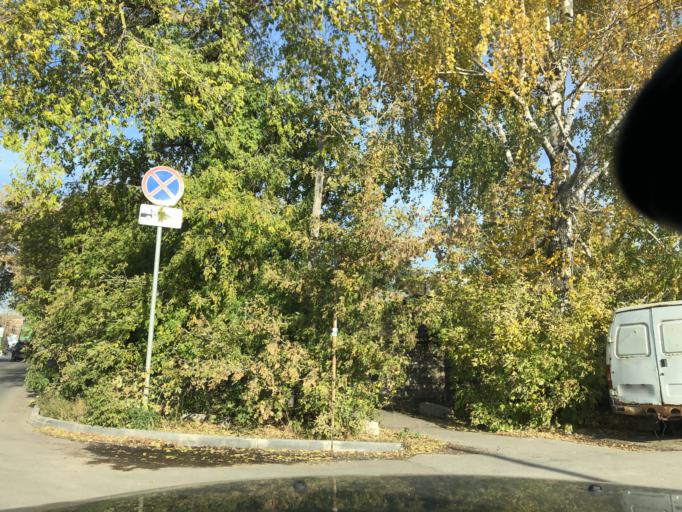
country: RU
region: Tula
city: Tula
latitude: 54.1908
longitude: 37.6295
